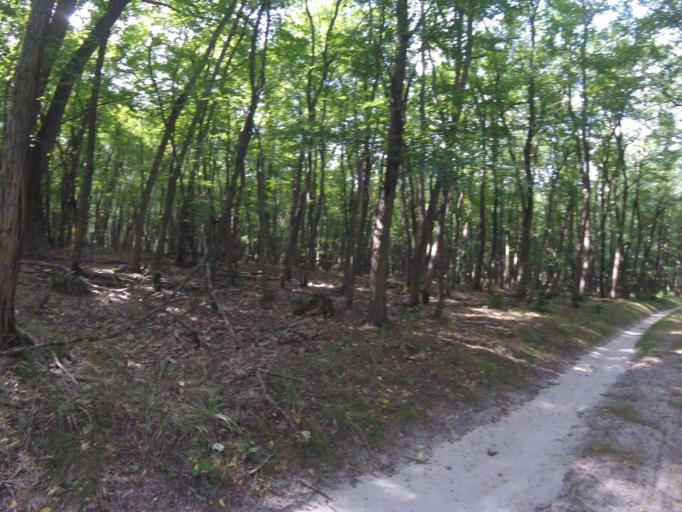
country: DE
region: Brandenburg
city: Mittenwalde
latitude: 52.2378
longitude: 13.5803
